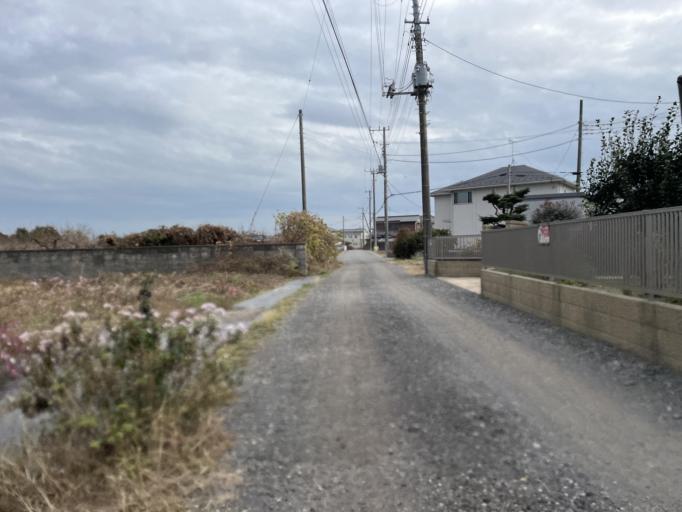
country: JP
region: Saitama
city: Shiraoka
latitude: 36.0215
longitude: 139.6420
